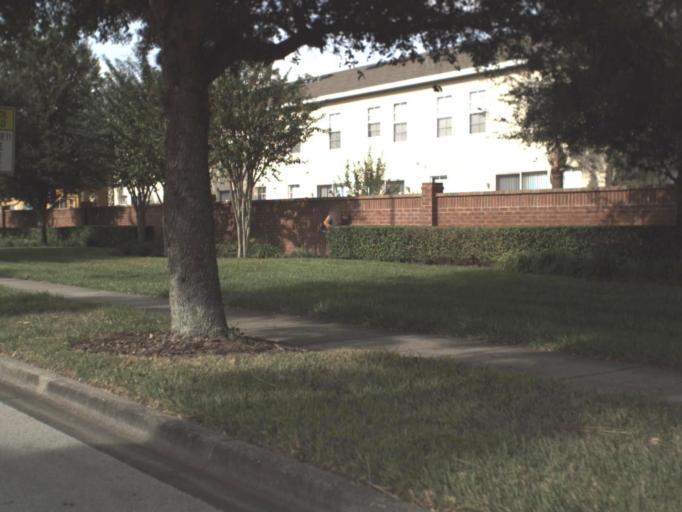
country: US
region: Florida
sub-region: Orange County
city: Conway
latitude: 28.4268
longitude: -81.2536
